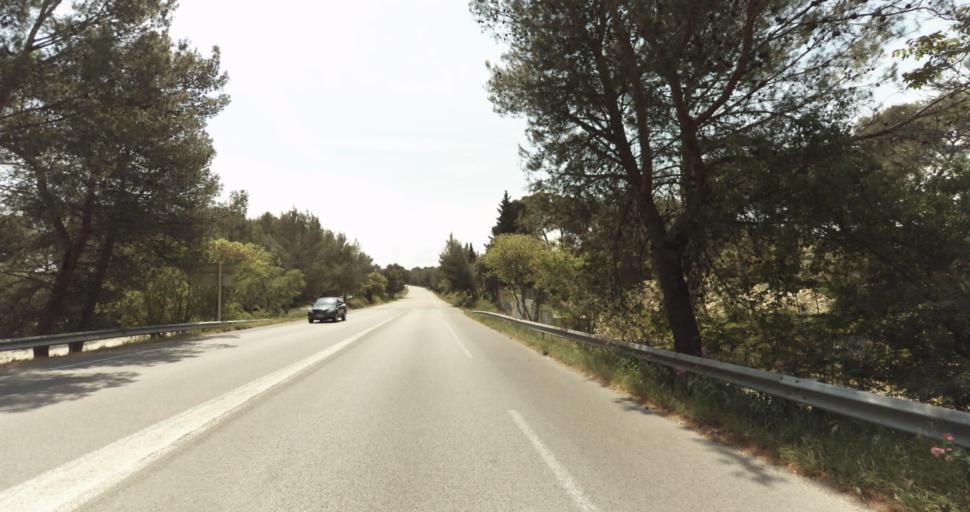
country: FR
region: Languedoc-Roussillon
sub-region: Departement du Gard
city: Nimes
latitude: 43.8659
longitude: 4.3236
